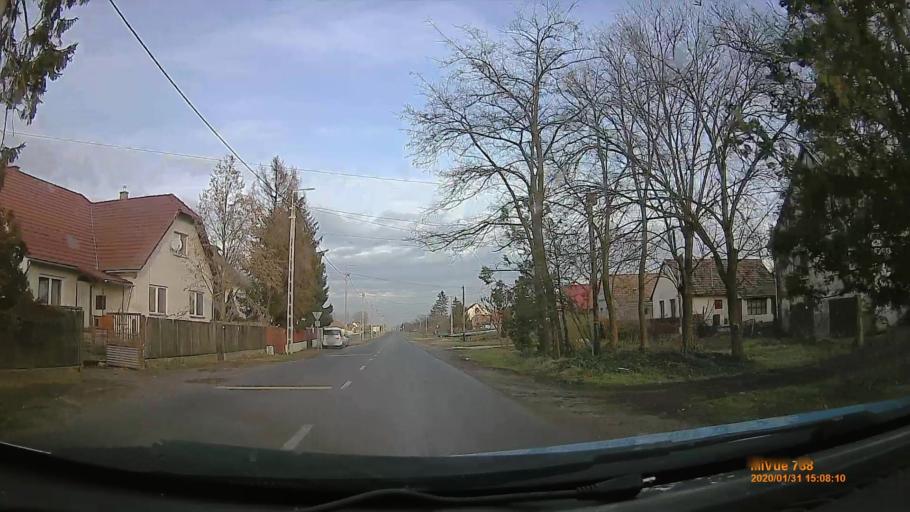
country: HU
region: Hajdu-Bihar
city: Polgar
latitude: 47.8647
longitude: 21.1294
